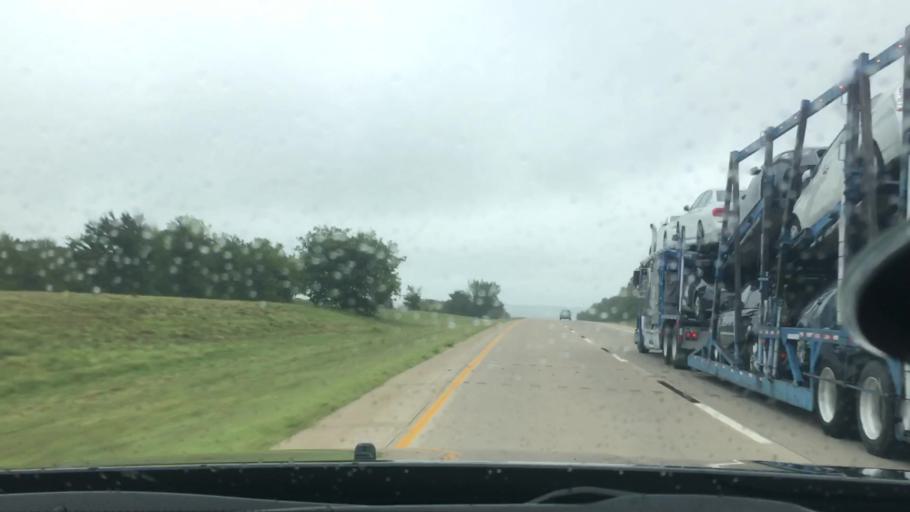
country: US
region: Oklahoma
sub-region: Okmulgee County
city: Henryetta
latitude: 35.4325
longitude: -95.9319
